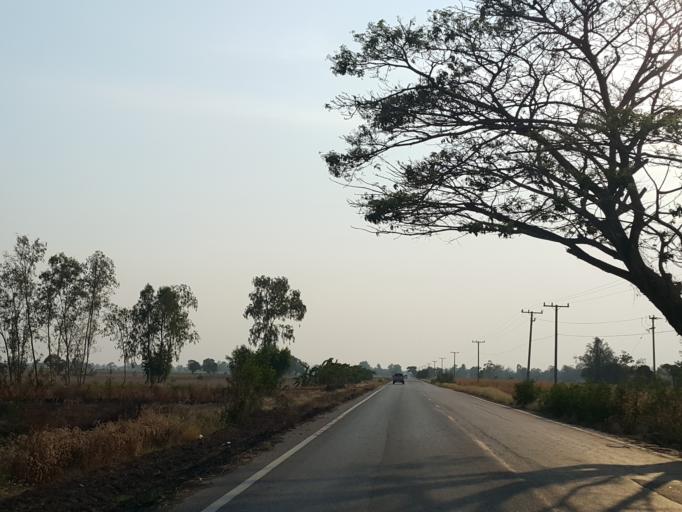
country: TH
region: Uttaradit
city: Phichai
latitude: 17.1979
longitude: 100.0268
